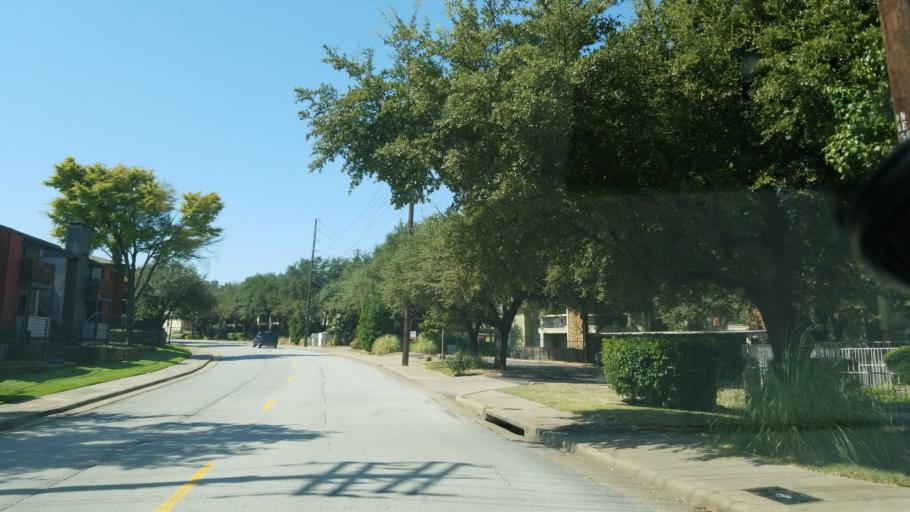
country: US
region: Texas
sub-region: Dallas County
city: Richardson
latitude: 32.9077
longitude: -96.7124
